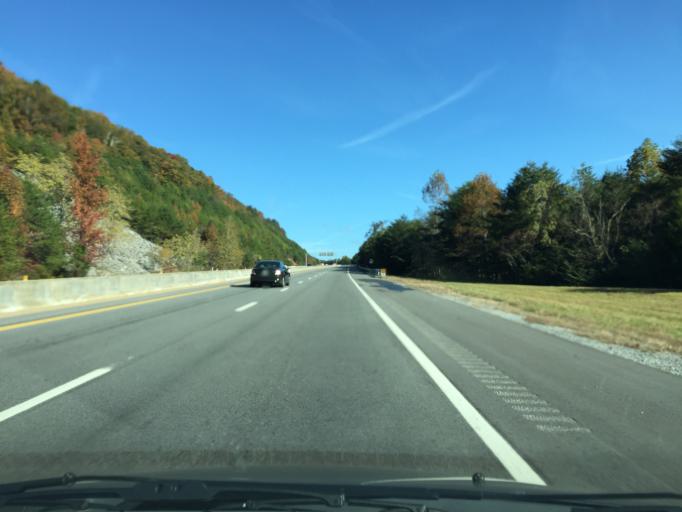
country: US
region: Tennessee
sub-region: Hamilton County
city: Soddy-Daisy
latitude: 35.3107
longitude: -85.1632
